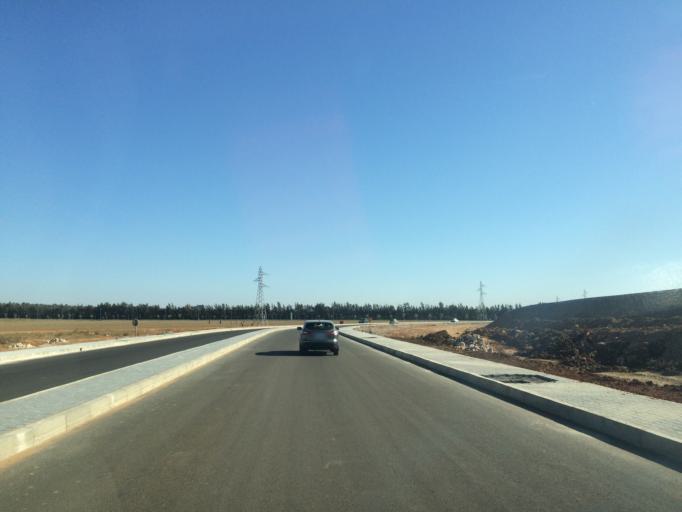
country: MA
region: Rabat-Sale-Zemmour-Zaer
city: Sale
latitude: 33.9832
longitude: -6.7314
